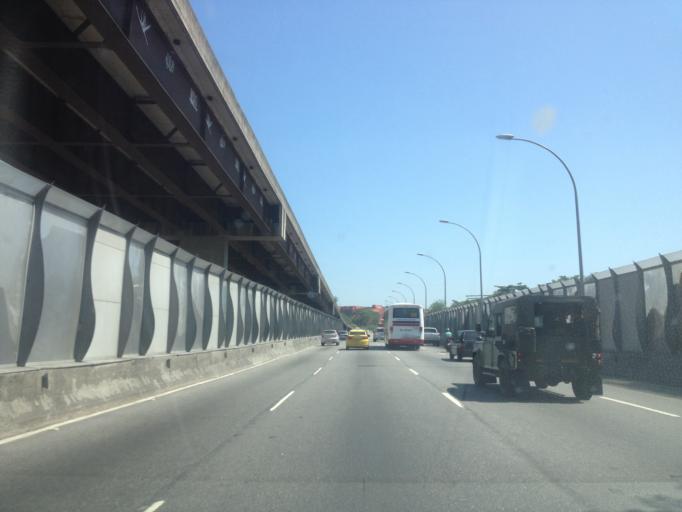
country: BR
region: Rio de Janeiro
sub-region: Rio De Janeiro
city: Rio de Janeiro
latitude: -22.8817
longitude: -43.2303
